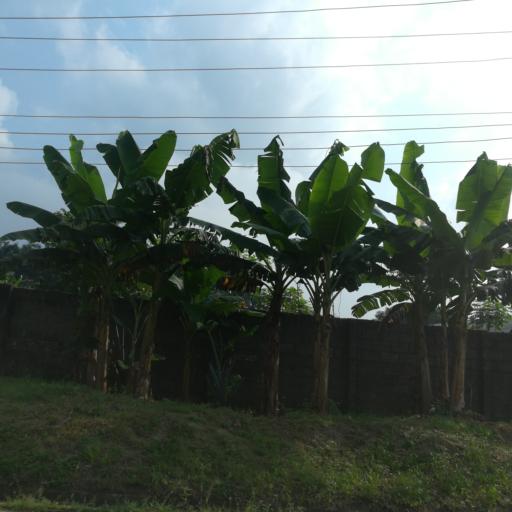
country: NG
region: Rivers
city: Okrika
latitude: 4.7754
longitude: 7.1582
